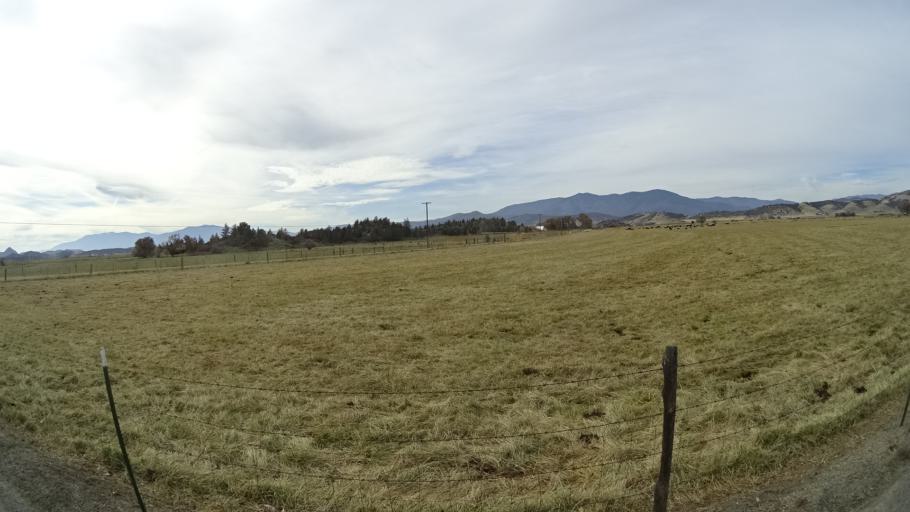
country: US
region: California
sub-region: Siskiyou County
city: Montague
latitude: 41.6626
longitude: -122.5022
